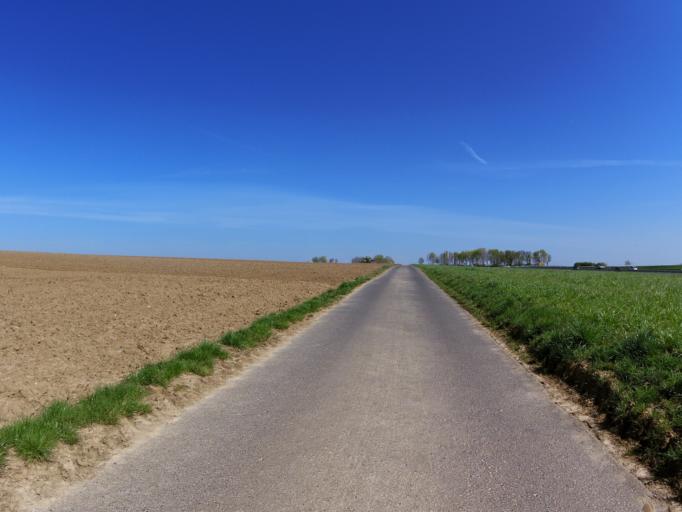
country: DE
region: Bavaria
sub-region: Regierungsbezirk Unterfranken
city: Kurnach
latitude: 49.8595
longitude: 10.0324
